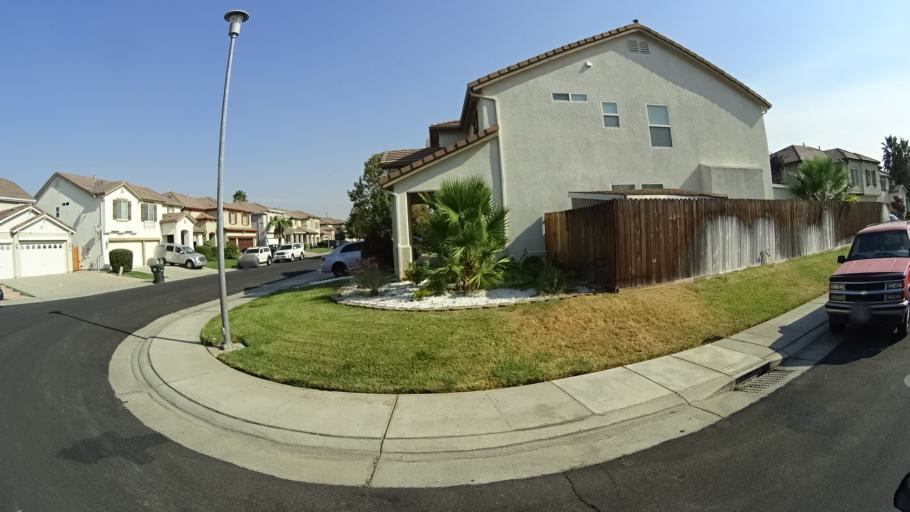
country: US
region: California
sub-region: Sacramento County
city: Laguna
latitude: 38.3867
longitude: -121.4355
